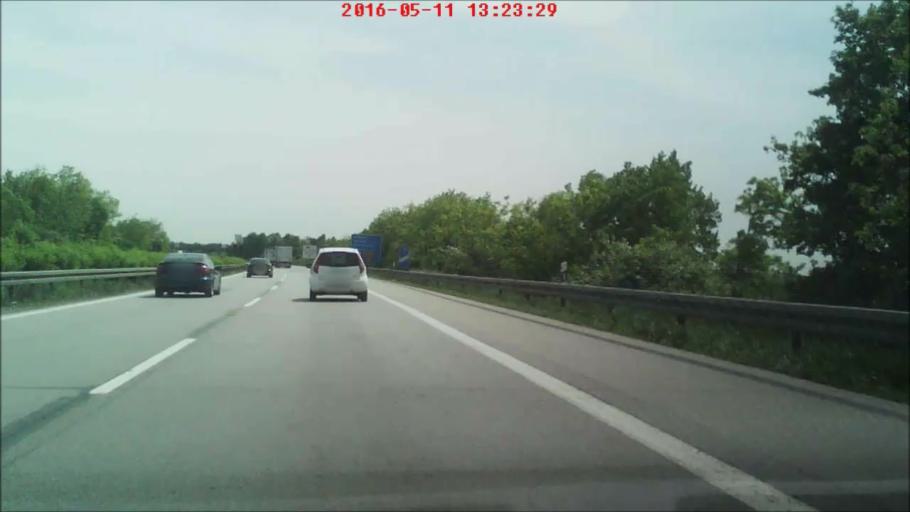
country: AT
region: Upper Austria
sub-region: Politischer Bezirk Scharding
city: Scharding
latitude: 48.4411
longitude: 13.3752
